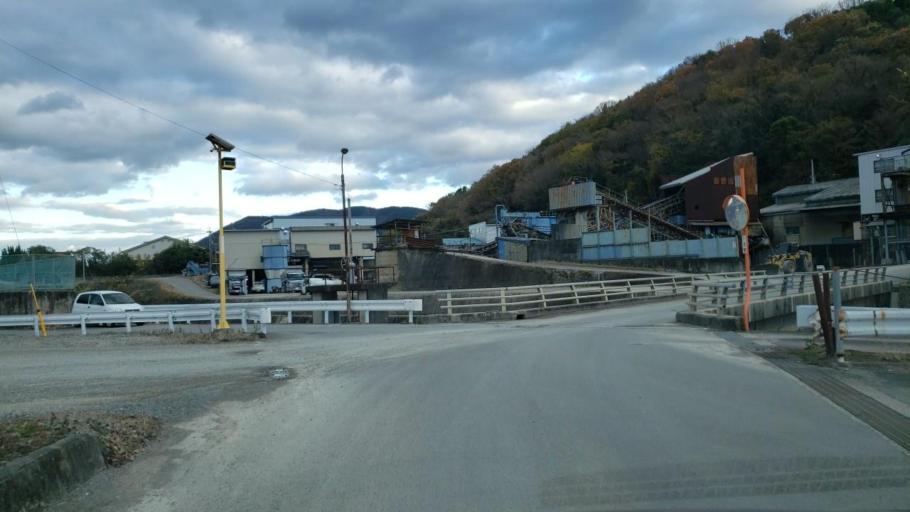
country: JP
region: Tokushima
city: Wakimachi
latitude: 34.0569
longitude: 134.1548
